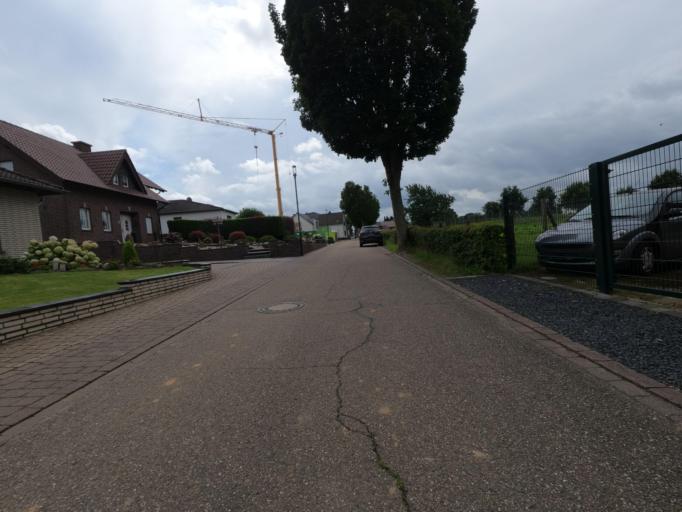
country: DE
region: North Rhine-Westphalia
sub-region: Regierungsbezirk Koln
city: Gangelt
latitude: 51.0054
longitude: 6.0241
